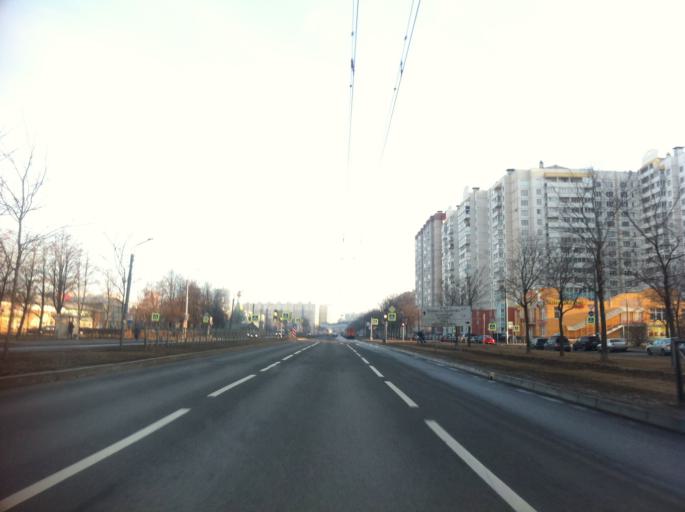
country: RU
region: St.-Petersburg
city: Uritsk
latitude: 59.8499
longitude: 30.1758
